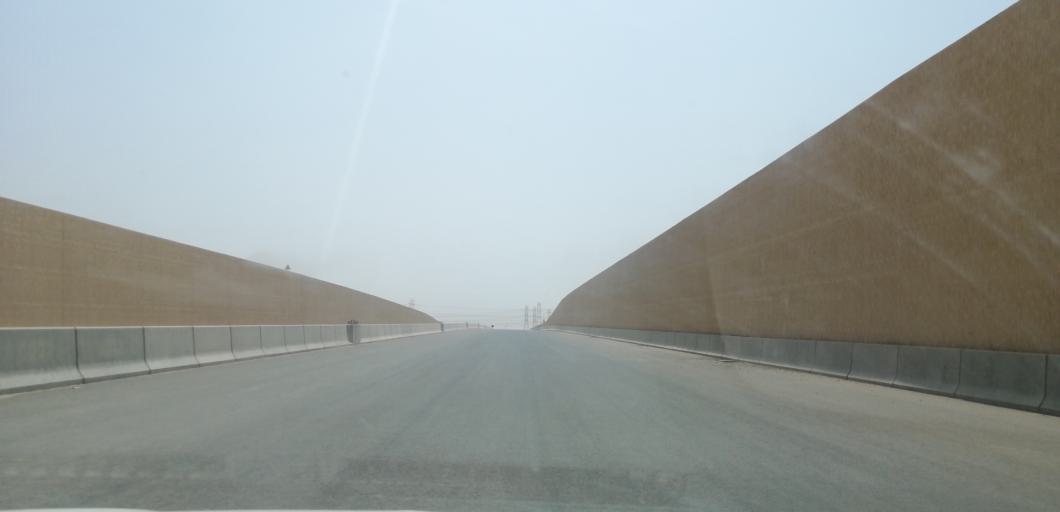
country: KW
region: Muhafazat al Jahra'
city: Al Jahra'
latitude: 29.4500
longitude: 47.6075
